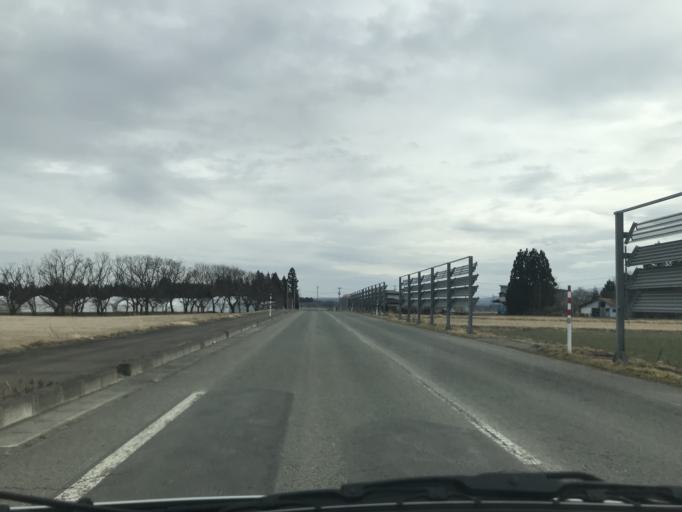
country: JP
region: Iwate
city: Kitakami
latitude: 39.3324
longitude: 140.9950
